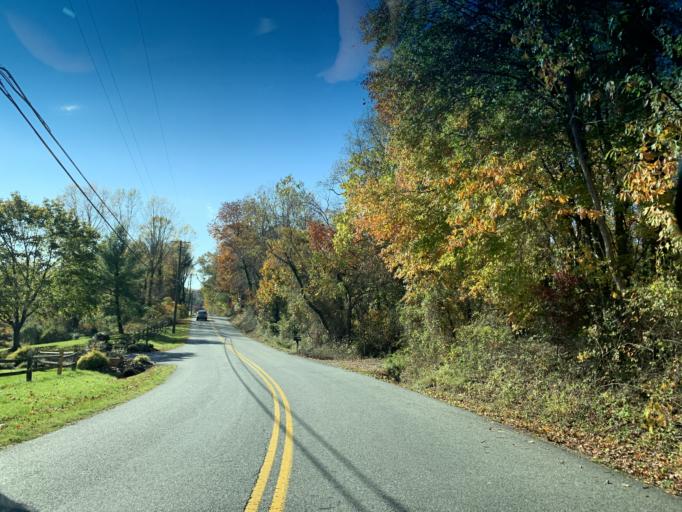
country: US
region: Maryland
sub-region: Harford County
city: Joppatowne
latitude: 39.4739
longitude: -76.3652
